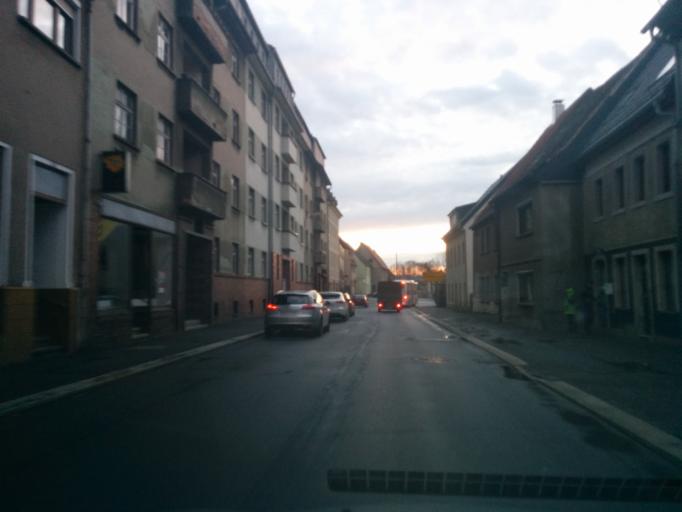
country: DE
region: Saxony
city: Frankenberg
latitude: 50.9094
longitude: 13.0300
